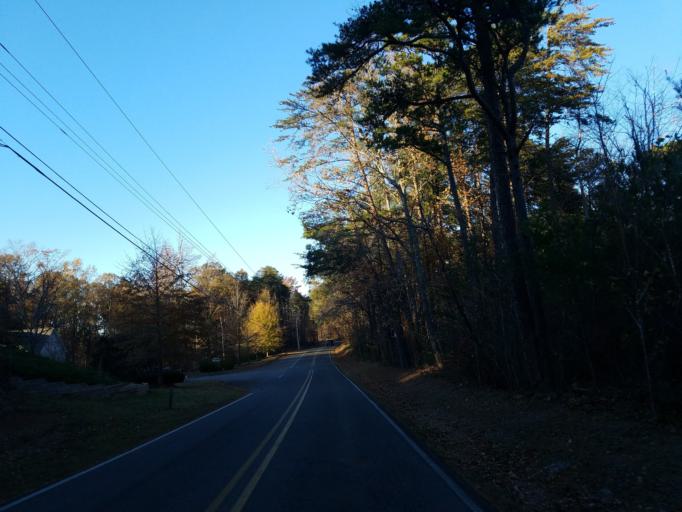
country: US
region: Georgia
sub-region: Pickens County
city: Nelson
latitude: 34.3938
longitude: -84.3723
